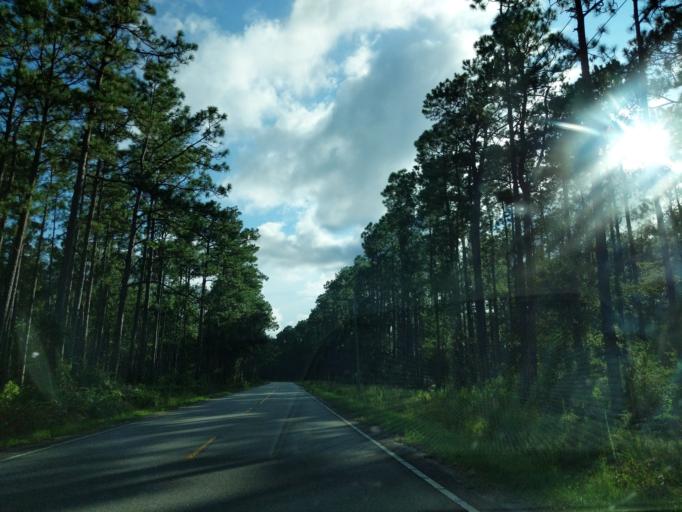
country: US
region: South Carolina
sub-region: Charleston County
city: Awendaw
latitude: 33.1333
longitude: -79.4412
